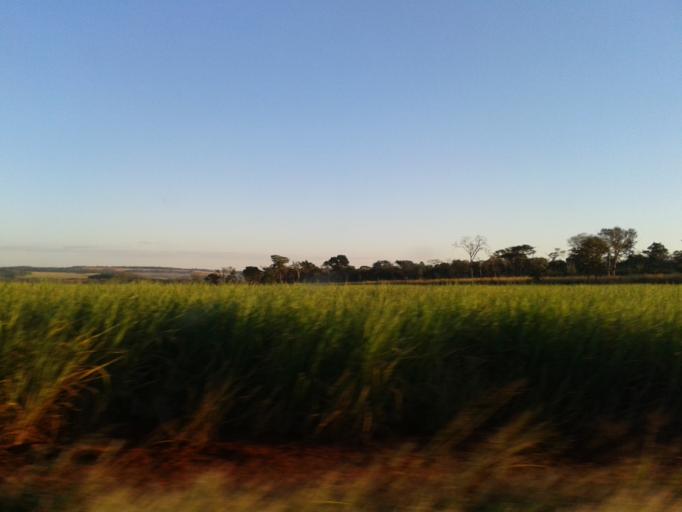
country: BR
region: Minas Gerais
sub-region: Centralina
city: Centralina
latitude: -18.6965
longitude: -49.3244
